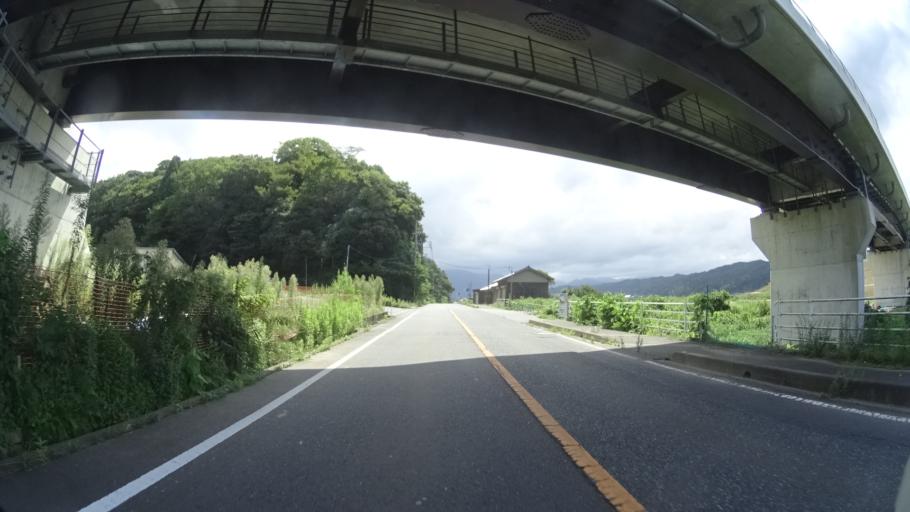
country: JP
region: Tottori
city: Tottori
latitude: 35.5016
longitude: 134.0804
